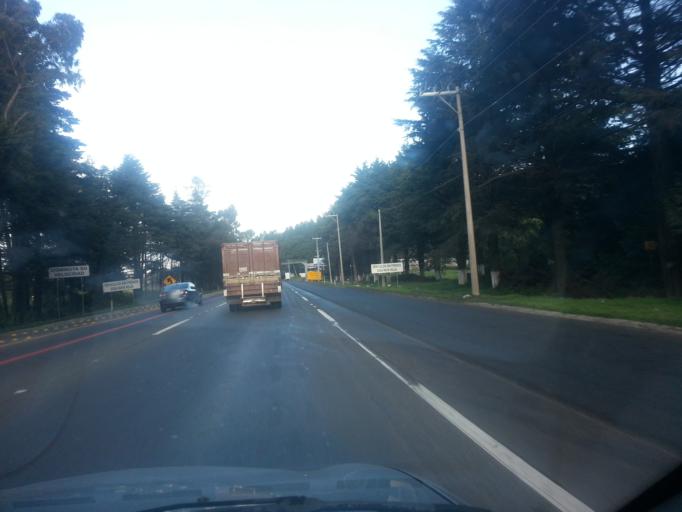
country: MX
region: Morelos
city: San Jeronimo Acazulco
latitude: 19.2968
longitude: -99.4152
